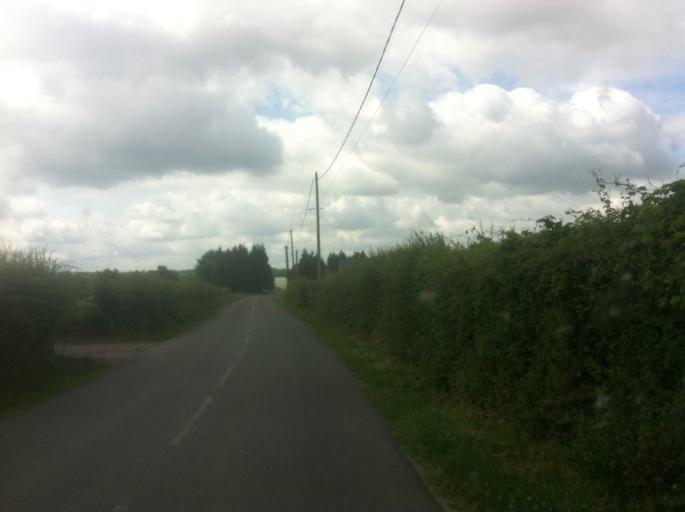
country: FR
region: Nord-Pas-de-Calais
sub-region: Departement du Nord
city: Sains-du-Nord
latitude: 50.1565
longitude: 4.0802
